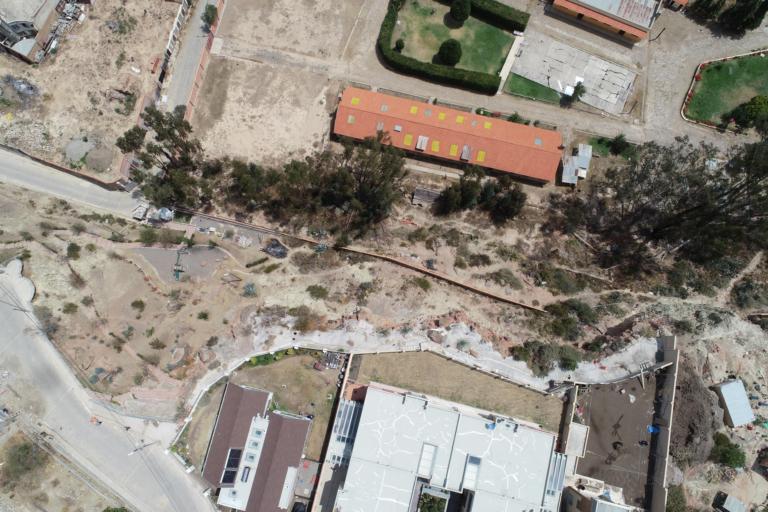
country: BO
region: La Paz
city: La Paz
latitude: -16.5592
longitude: -68.0926
